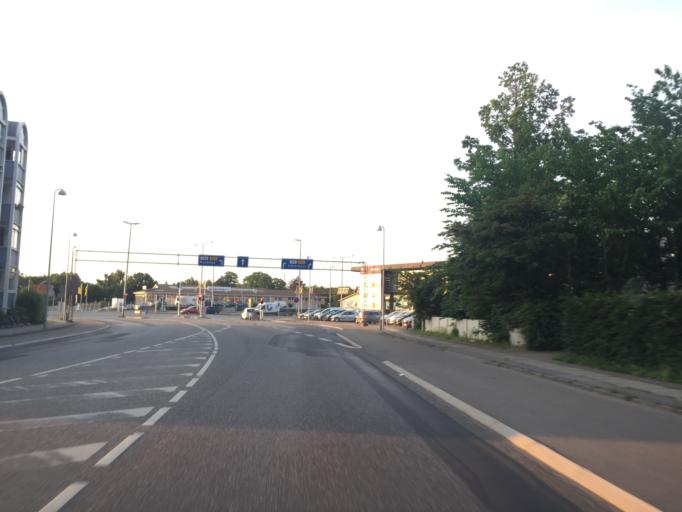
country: DK
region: Capital Region
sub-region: Hoje-Taastrup Kommune
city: Taastrup
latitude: 55.6578
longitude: 12.3087
